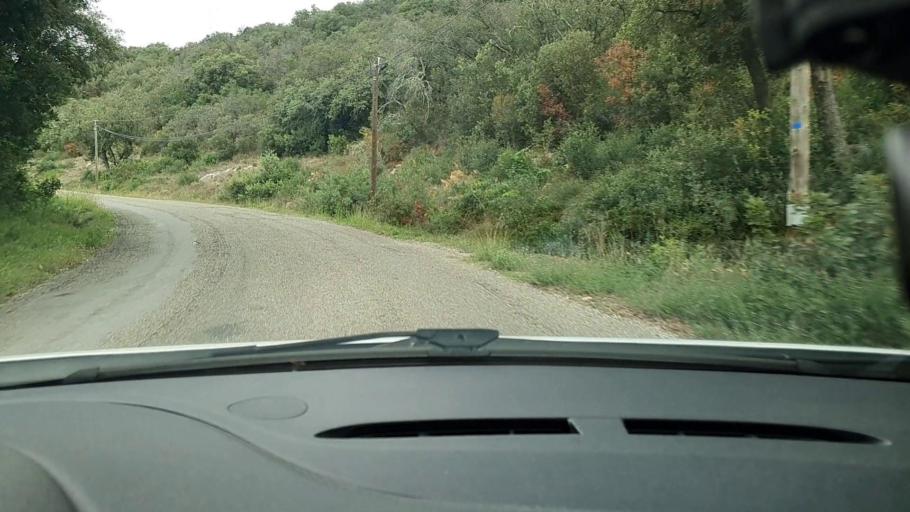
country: FR
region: Languedoc-Roussillon
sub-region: Departement du Gard
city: Montaren-et-Saint-Mediers
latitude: 44.0613
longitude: 4.3198
